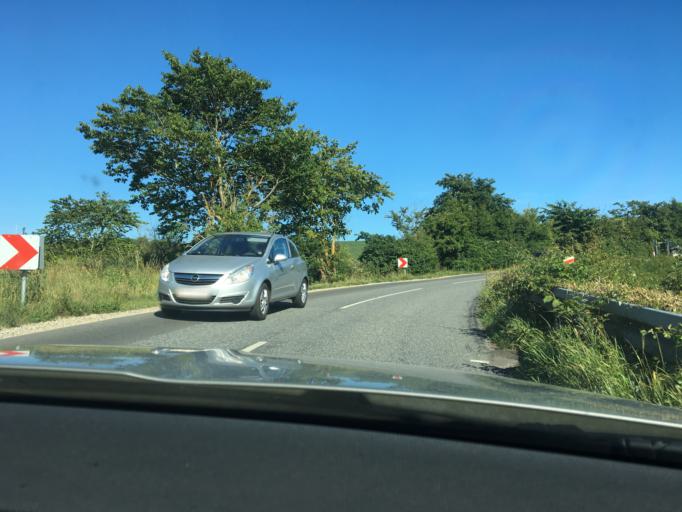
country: DK
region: Central Jutland
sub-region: Syddjurs Kommune
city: Hornslet
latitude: 56.3095
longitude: 10.3426
